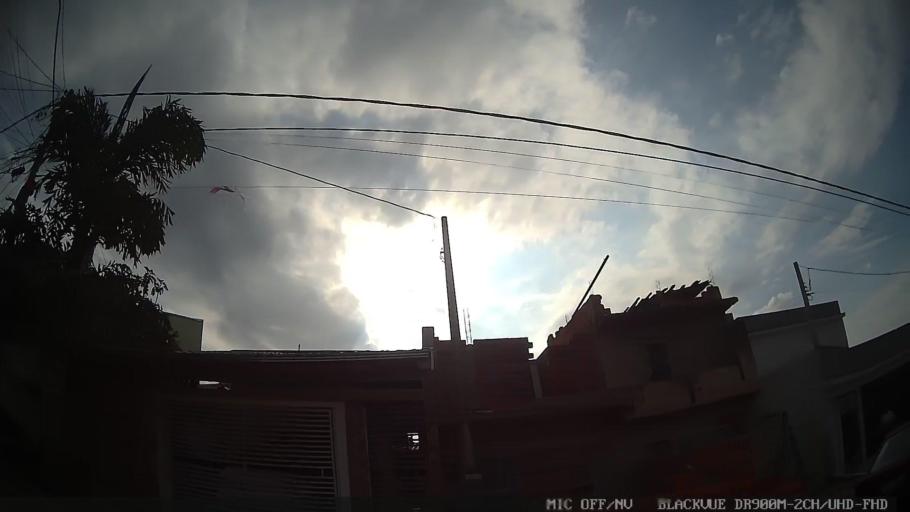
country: BR
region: Sao Paulo
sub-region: Indaiatuba
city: Indaiatuba
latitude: -23.0990
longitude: -47.2408
